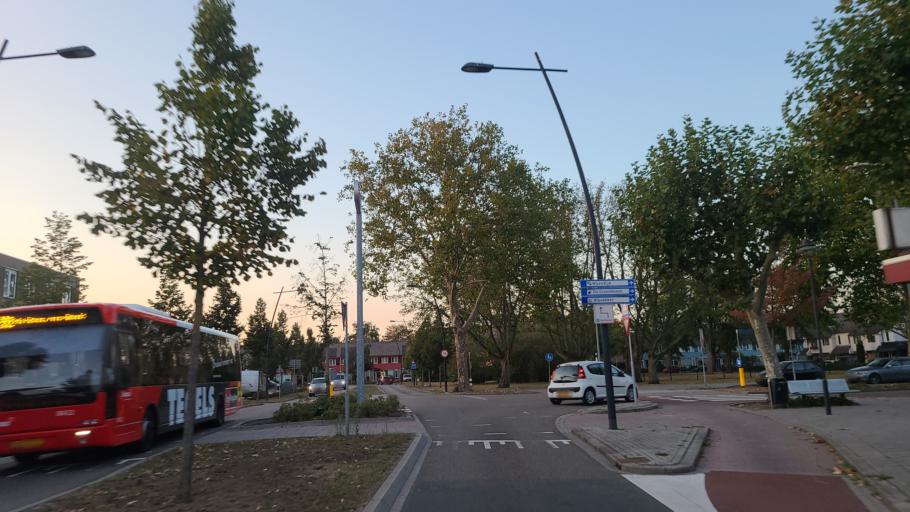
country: NL
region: North Brabant
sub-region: Gemeente Uden
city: Uden
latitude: 51.6692
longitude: 5.6121
